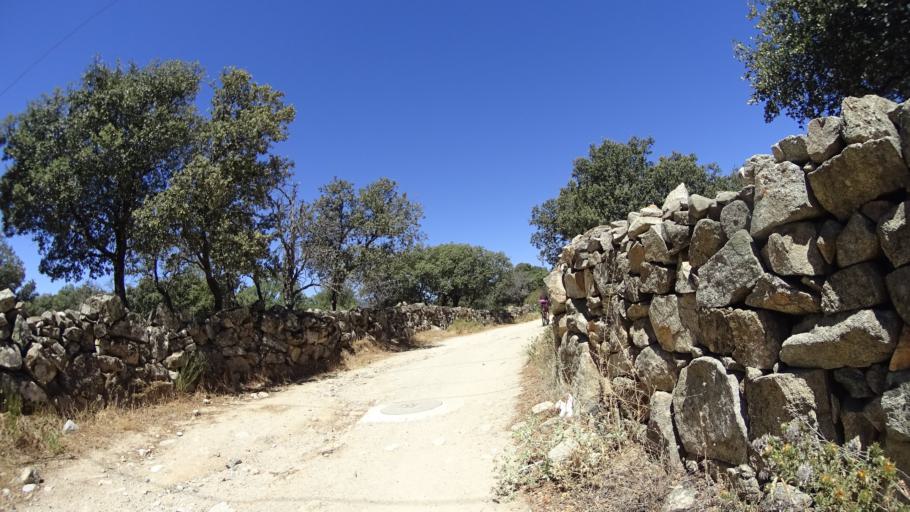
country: ES
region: Madrid
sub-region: Provincia de Madrid
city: Collado Mediano
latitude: 40.6782
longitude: -4.0405
